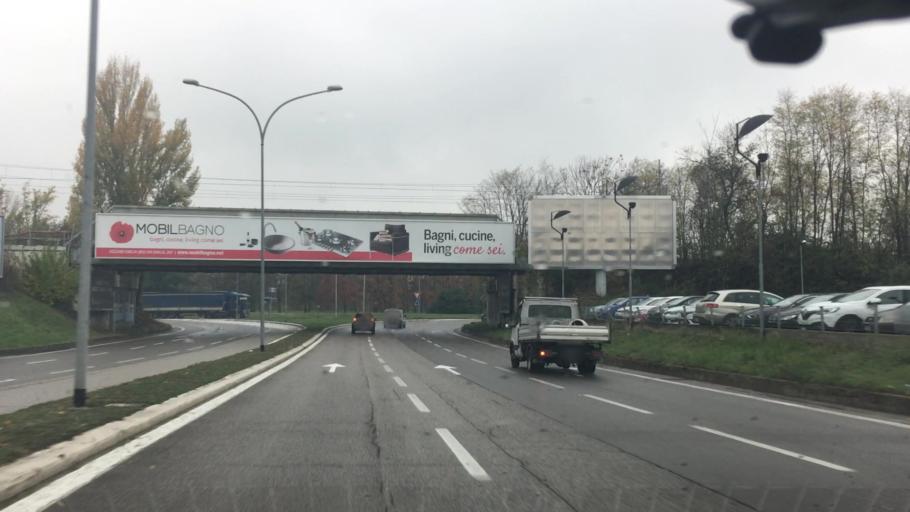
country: IT
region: Emilia-Romagna
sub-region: Provincia di Bologna
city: Casalecchio di Reno
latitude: 44.5091
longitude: 11.2787
